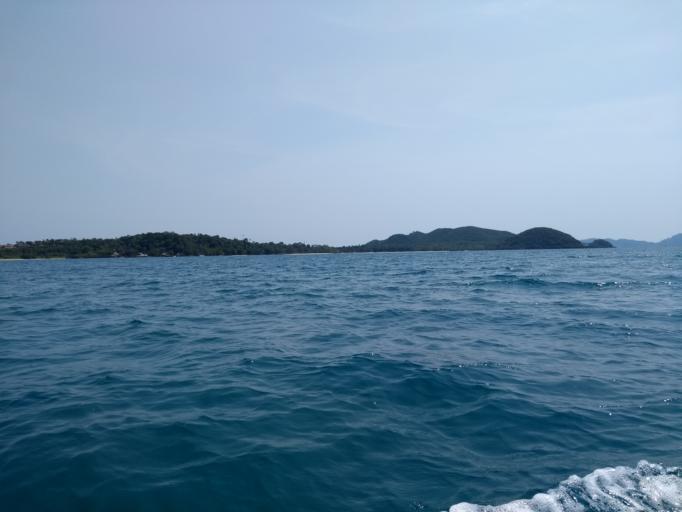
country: TH
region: Trat
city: Ko Kut
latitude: 11.8300
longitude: 102.4646
